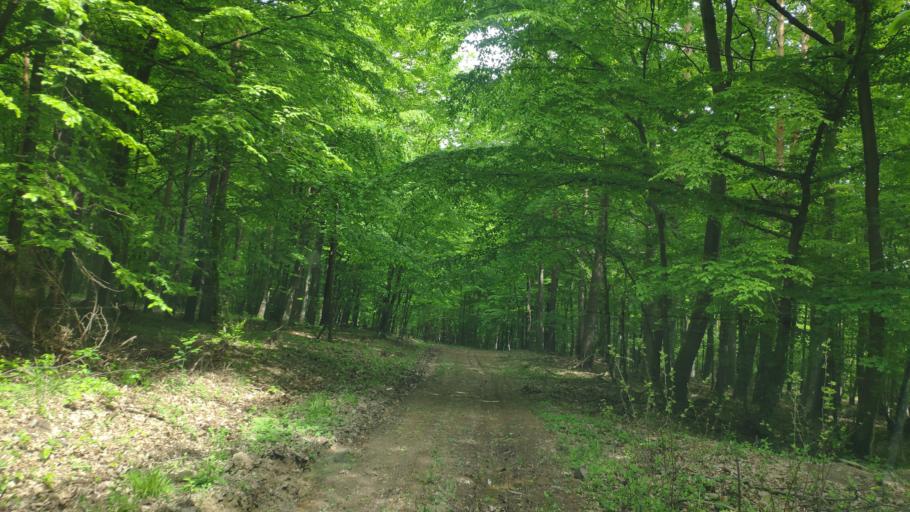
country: SK
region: Kosicky
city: Secovce
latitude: 48.7037
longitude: 21.5848
